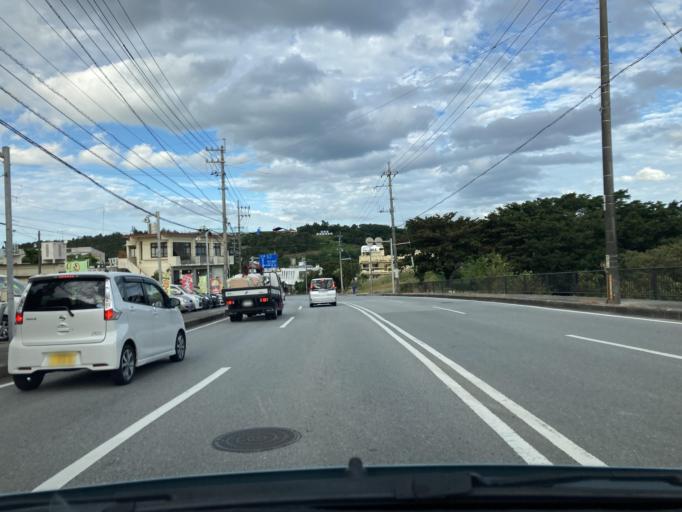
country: JP
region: Okinawa
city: Ishikawa
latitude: 26.3903
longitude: 127.8314
